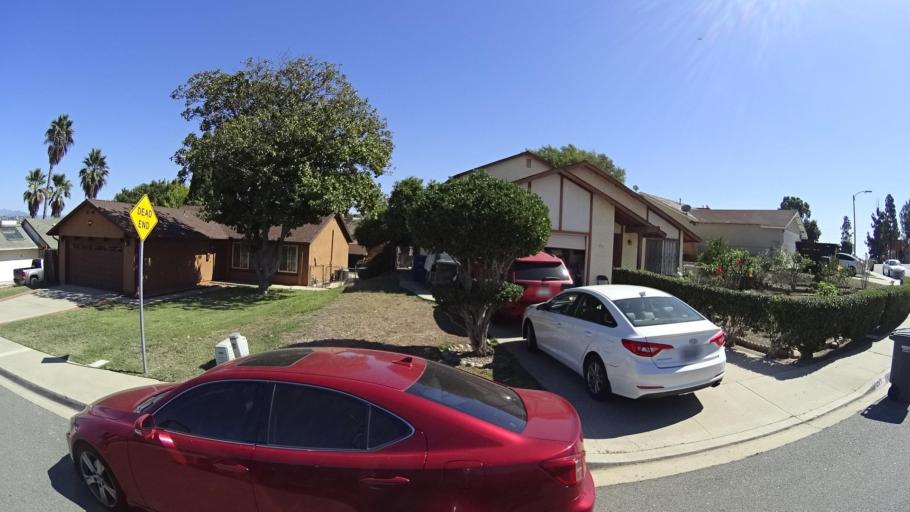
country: US
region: California
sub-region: San Diego County
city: La Presa
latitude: 32.6992
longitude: -117.0193
